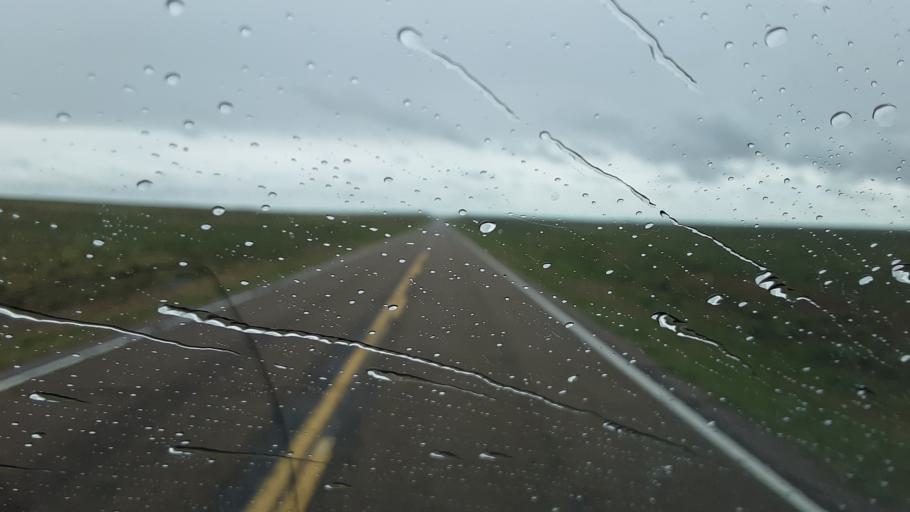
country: US
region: Colorado
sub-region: Lincoln County
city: Hugo
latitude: 38.8494
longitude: -103.2603
